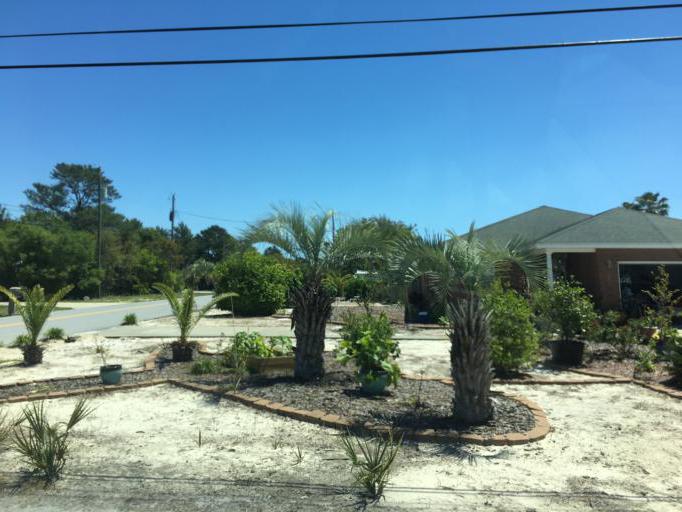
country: US
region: Florida
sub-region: Bay County
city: Laguna Beach
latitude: 30.2653
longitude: -85.9664
